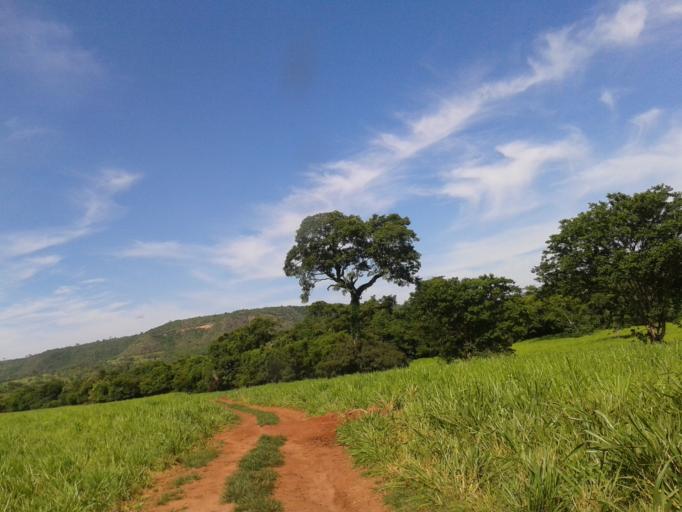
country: BR
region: Minas Gerais
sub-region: Santa Vitoria
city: Santa Vitoria
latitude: -19.0812
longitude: -50.0172
